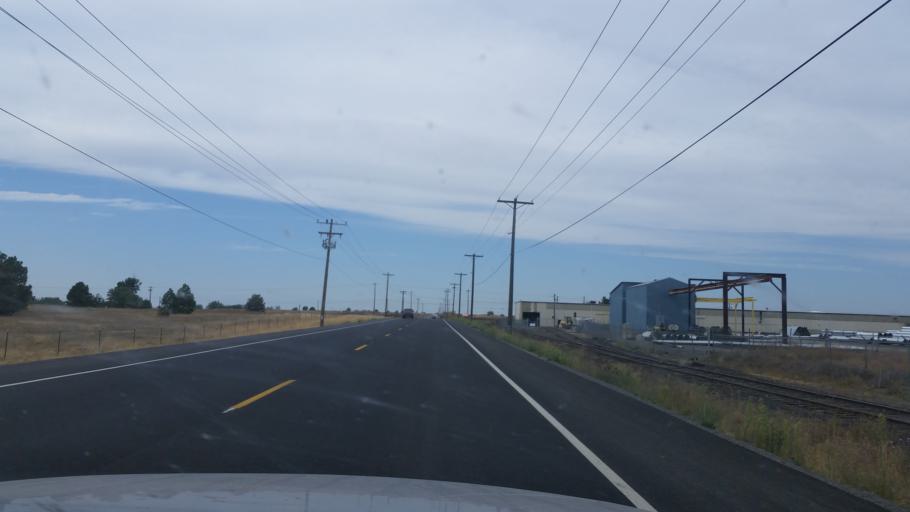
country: US
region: Washington
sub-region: Spokane County
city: Airway Heights
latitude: 47.6284
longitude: -117.5994
